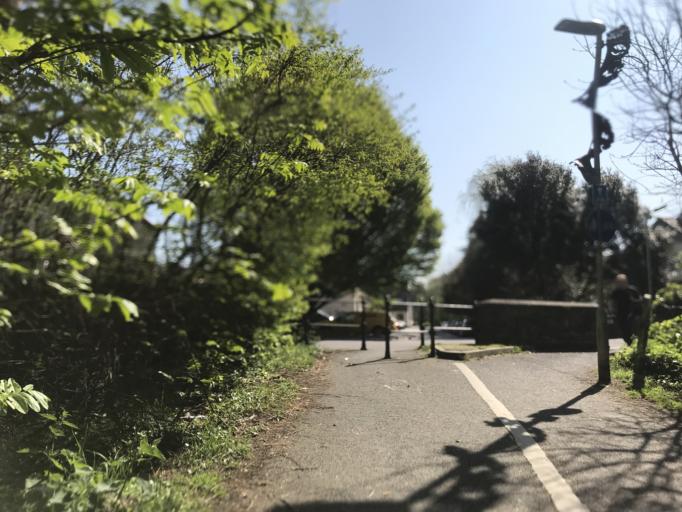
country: GB
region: England
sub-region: Devon
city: Barnstaple
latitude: 51.0748
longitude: -4.0491
